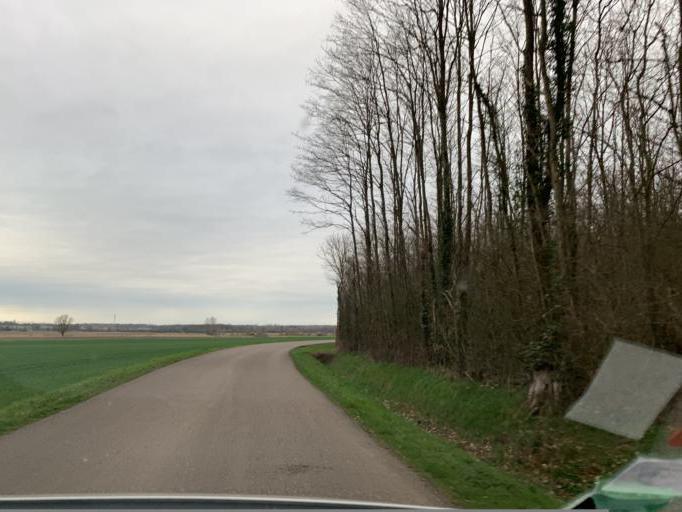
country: FR
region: Rhone-Alpes
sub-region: Departement de l'Ain
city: Mionnay
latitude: 45.8757
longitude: 4.9413
